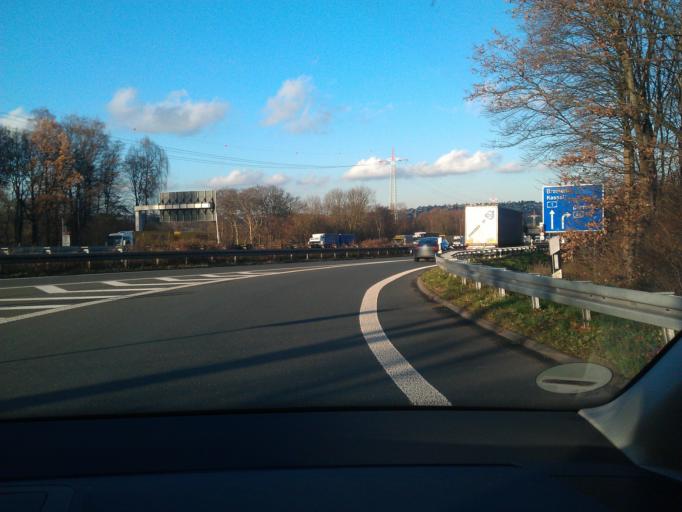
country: DE
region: North Rhine-Westphalia
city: Schwerte
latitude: 51.4312
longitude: 7.5323
